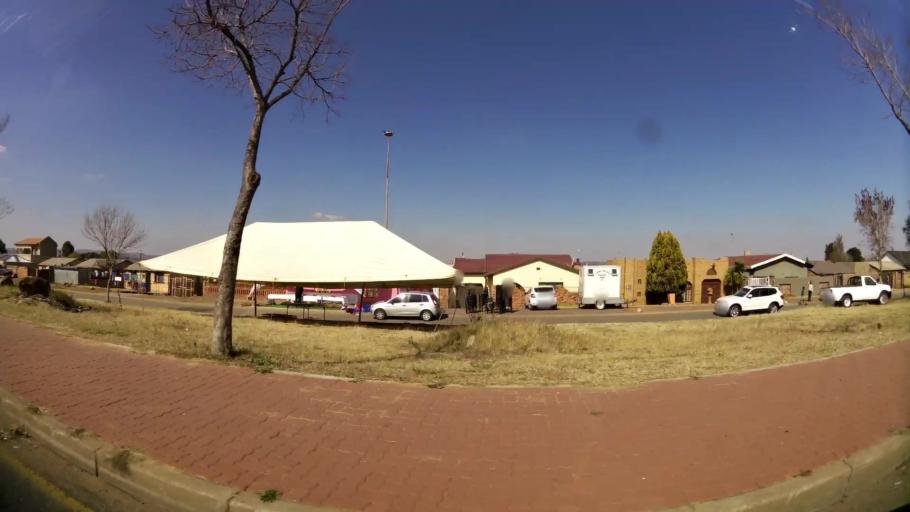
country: ZA
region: Gauteng
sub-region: City of Johannesburg Metropolitan Municipality
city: Soweto
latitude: -26.2756
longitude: 27.8693
